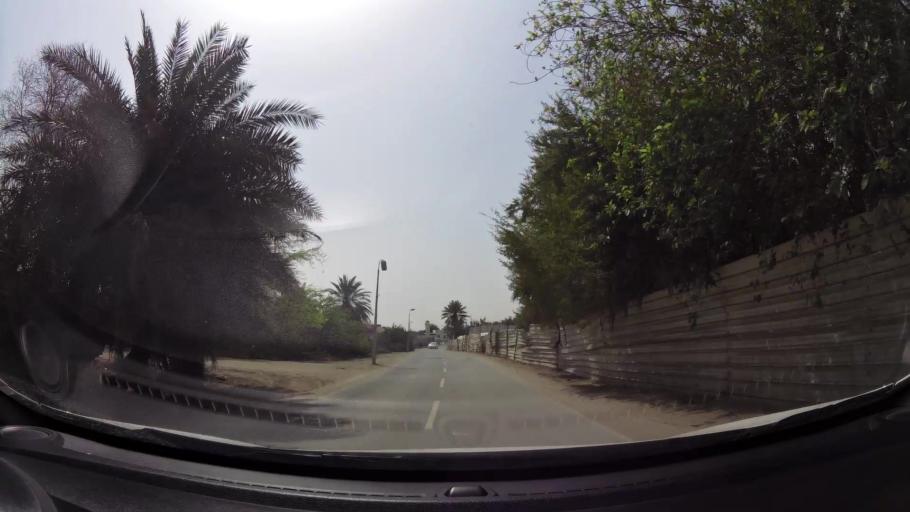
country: BH
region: Manama
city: Jidd Hafs
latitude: 26.2330
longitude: 50.5015
